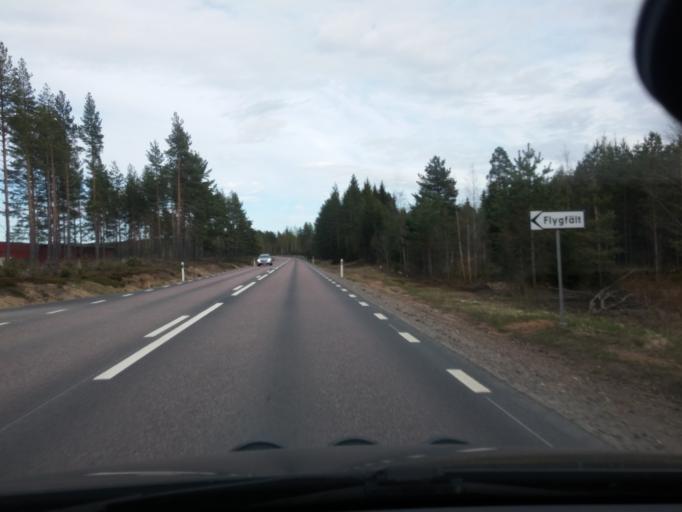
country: SE
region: Gaevleborg
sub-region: Ljusdals Kommun
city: Ljusdal
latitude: 61.8162
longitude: 16.0030
